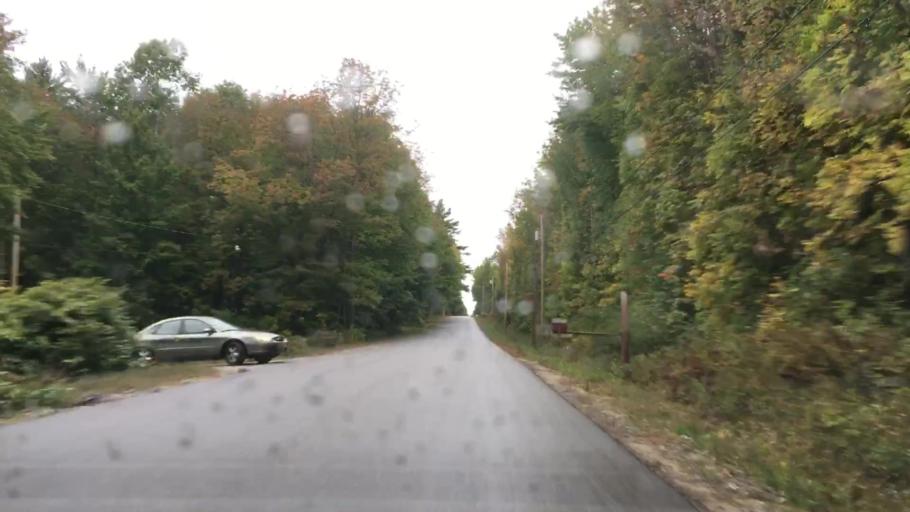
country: US
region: Maine
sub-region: Cumberland County
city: Harrison
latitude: 44.0921
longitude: -70.6550
